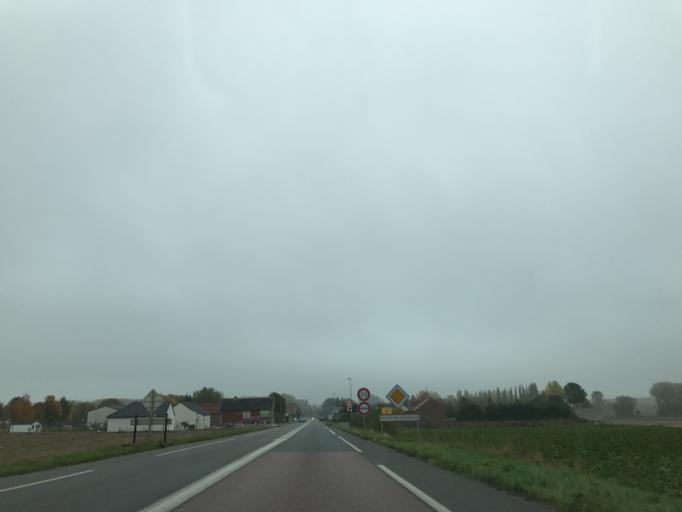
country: FR
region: Nord-Pas-de-Calais
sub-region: Departement du Pas-de-Calais
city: Beaurains
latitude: 50.2213
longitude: 2.8097
